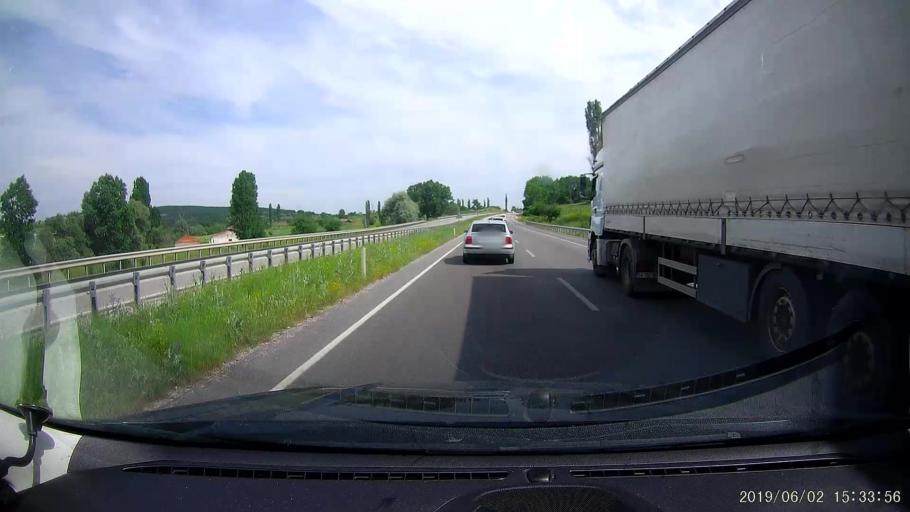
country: TR
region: Amasya
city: Saraycik
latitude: 40.9193
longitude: 35.1686
